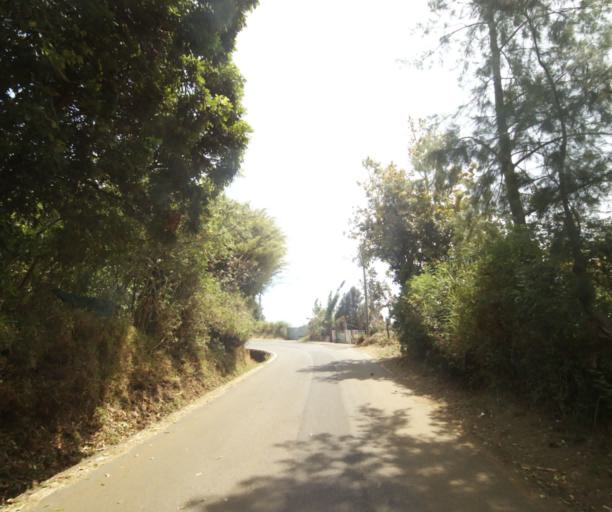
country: RE
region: Reunion
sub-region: Reunion
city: Trois-Bassins
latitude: -21.0645
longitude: 55.3075
